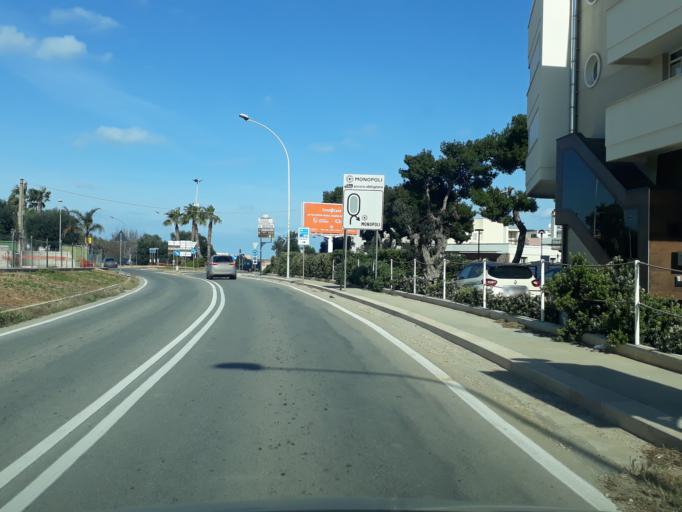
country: IT
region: Apulia
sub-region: Provincia di Bari
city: Monopoli
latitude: 40.9611
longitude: 17.2813
